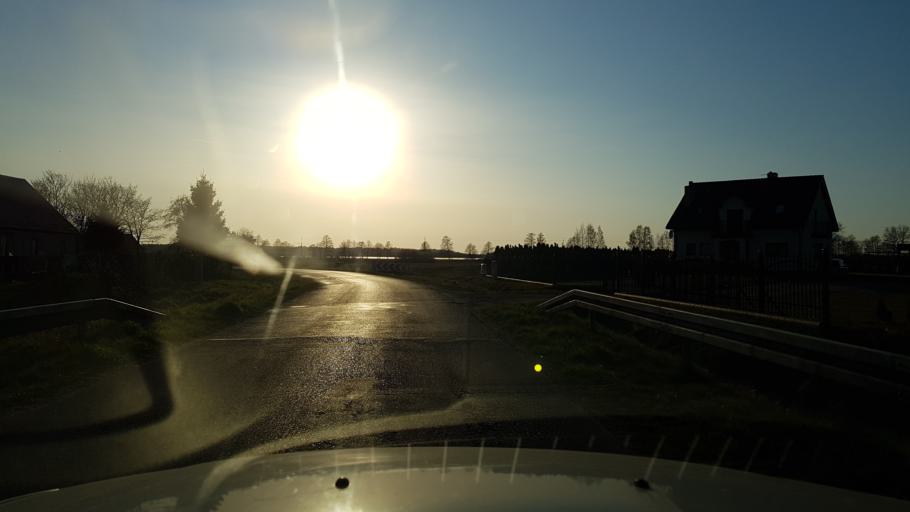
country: PL
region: West Pomeranian Voivodeship
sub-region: Powiat bialogardzki
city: Bialogard
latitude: 54.0468
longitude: 16.0087
